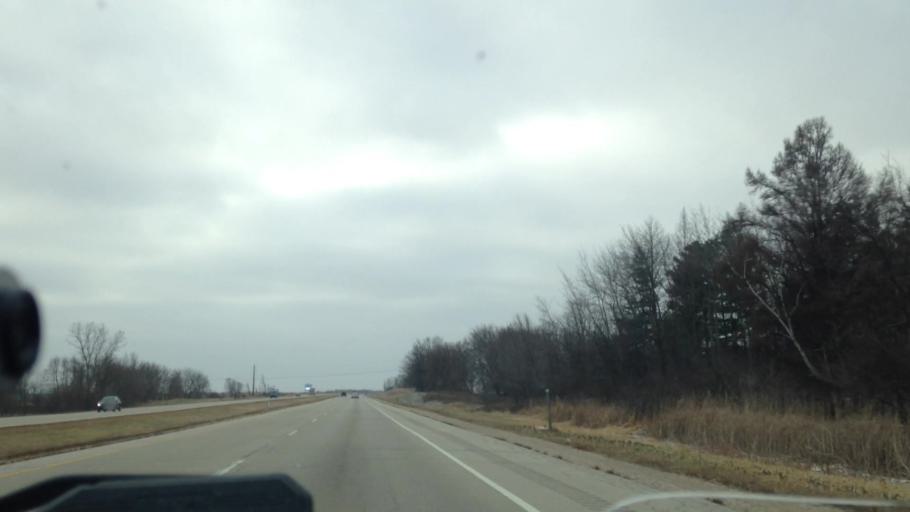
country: US
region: Wisconsin
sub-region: Washington County
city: Jackson
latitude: 43.3672
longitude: -88.1936
